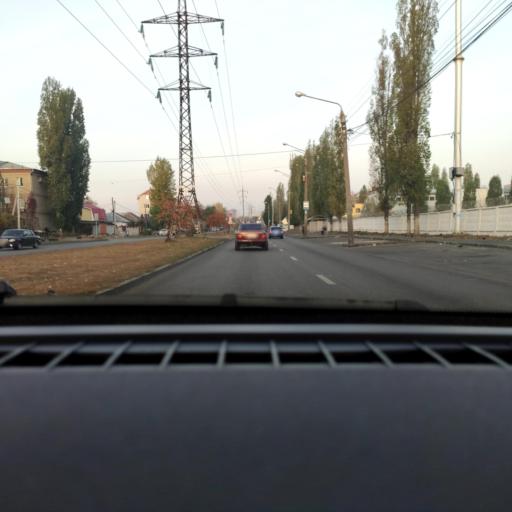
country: RU
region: Voronezj
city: Voronezh
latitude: 51.6334
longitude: 39.1794
